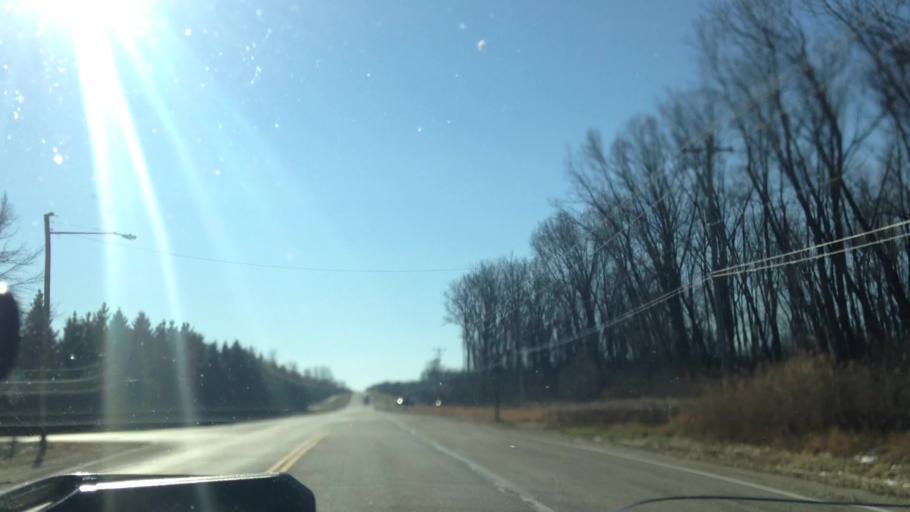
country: US
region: Wisconsin
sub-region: Washington County
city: Germantown
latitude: 43.2143
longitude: -88.1425
